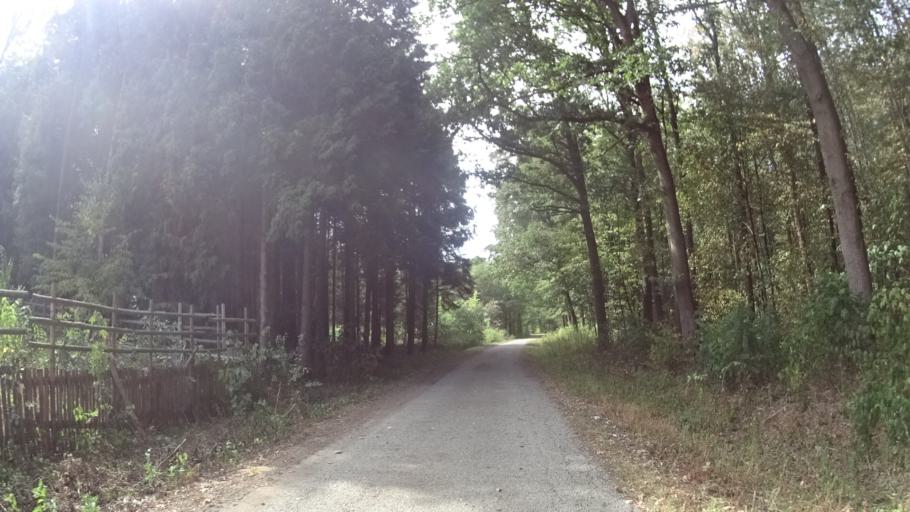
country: CZ
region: Olomoucky
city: Naklo
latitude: 49.6895
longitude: 17.1153
